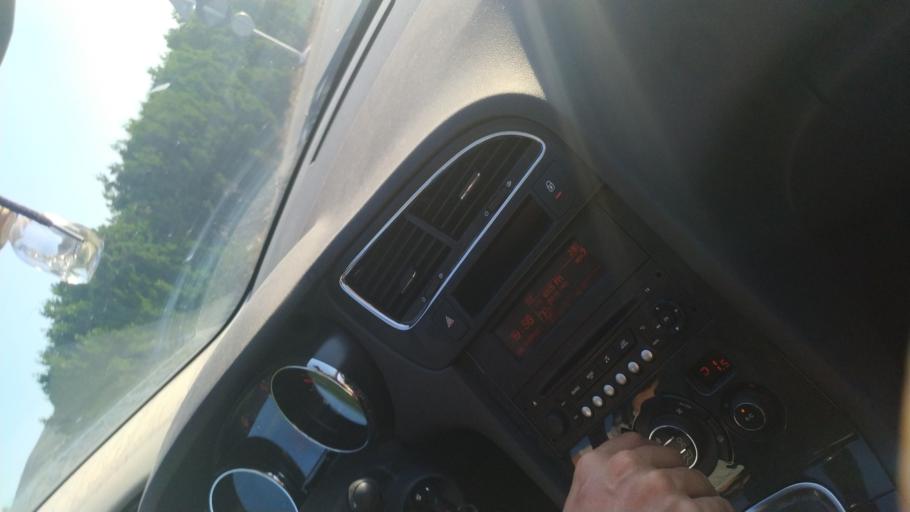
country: ES
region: Valencia
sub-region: Provincia de Alicante
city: Javea
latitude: 38.7753
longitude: 0.1289
